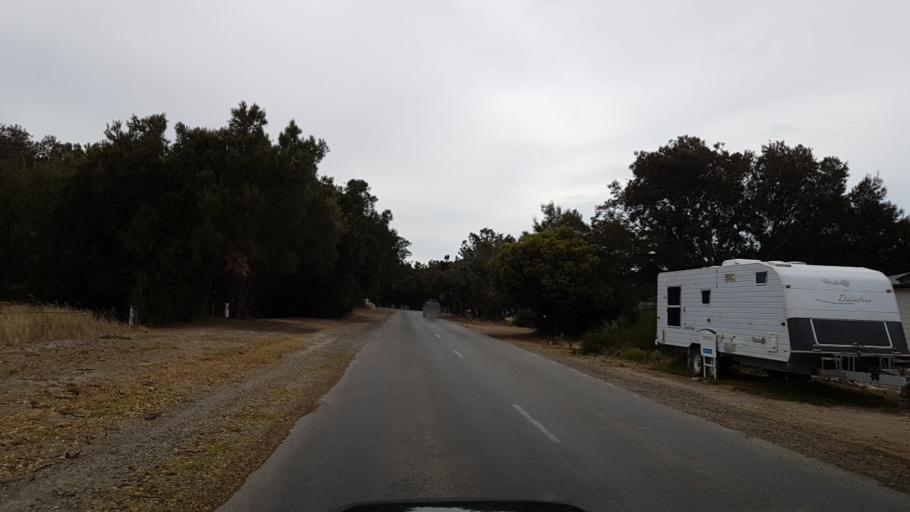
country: AU
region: South Australia
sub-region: Yorke Peninsula
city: Port Victoria
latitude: -34.9244
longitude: 137.0799
